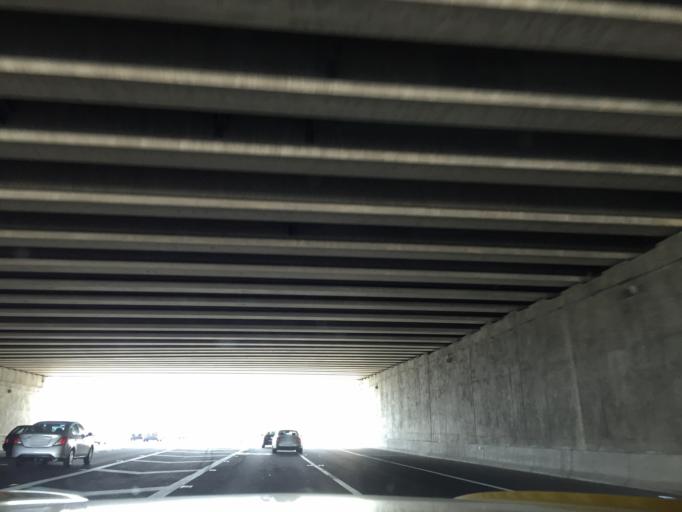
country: US
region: Virginia
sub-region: City of Alexandria
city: Alexandria
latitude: 38.7939
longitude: -77.0491
